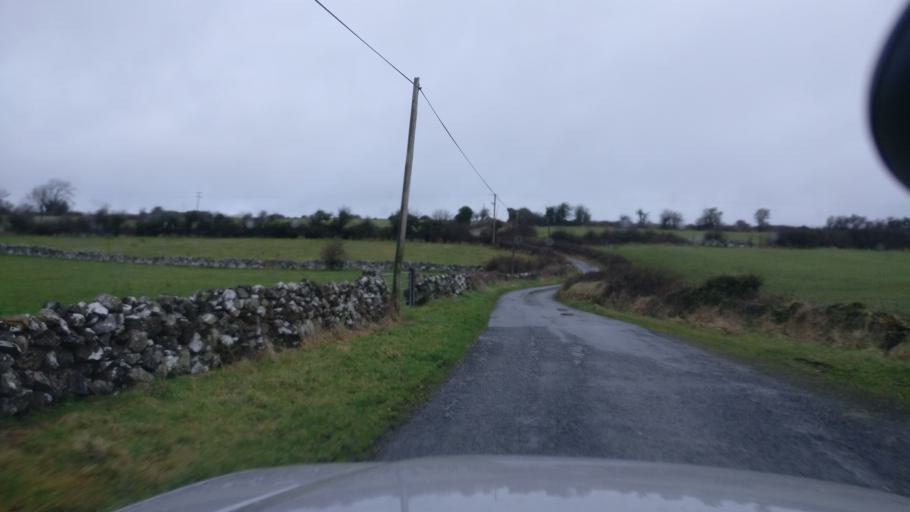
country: IE
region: Connaught
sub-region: County Galway
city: Loughrea
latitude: 53.1588
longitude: -8.6106
